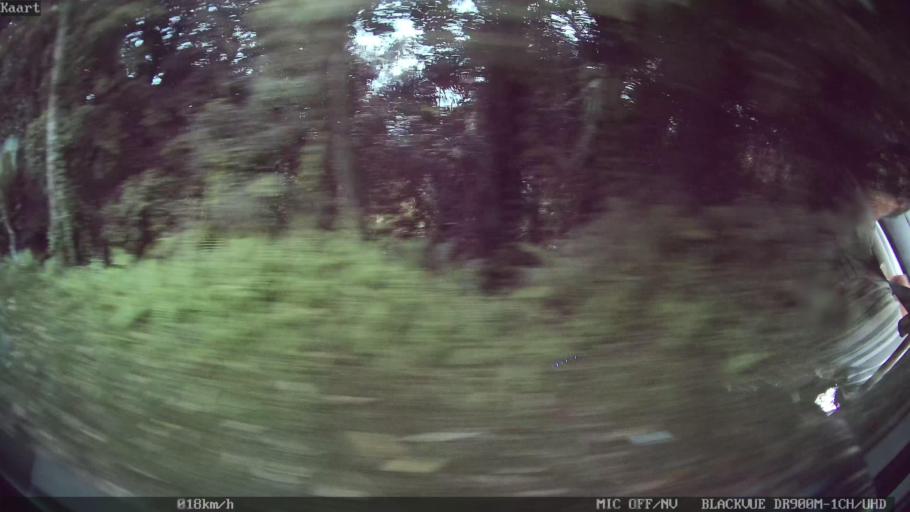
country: ID
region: Bali
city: Petang
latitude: -8.4160
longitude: 115.2245
